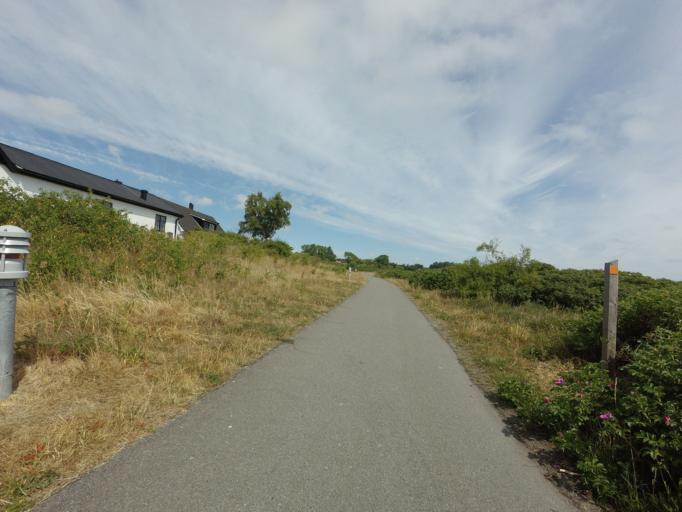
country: SE
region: Skane
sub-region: Simrishamns Kommun
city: Simrishamn
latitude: 55.5228
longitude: 14.3475
